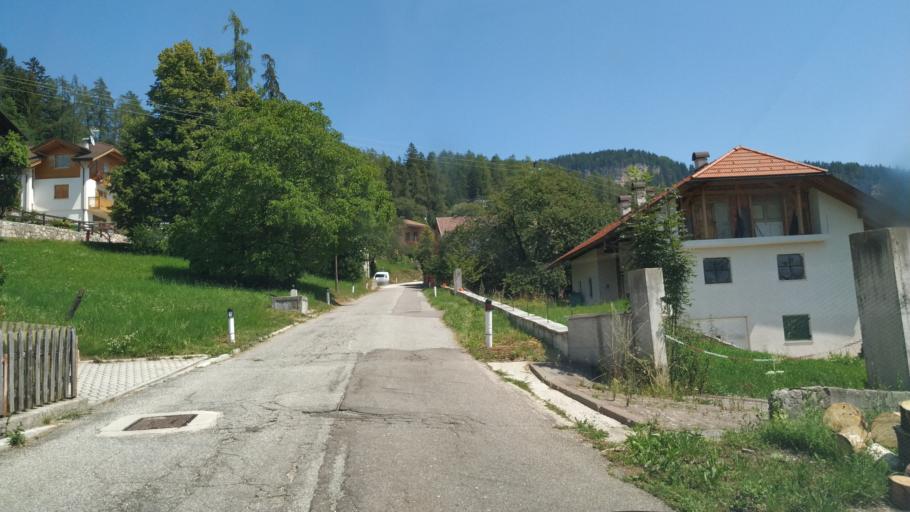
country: IT
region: Trentino-Alto Adige
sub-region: Bolzano
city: San Felice
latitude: 46.4809
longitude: 11.1390
